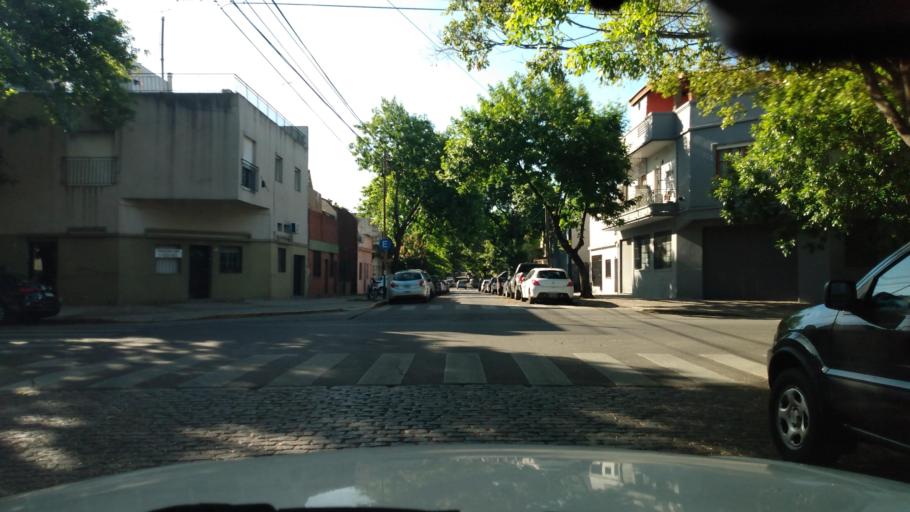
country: AR
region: Buenos Aires F.D.
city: Villa Santa Rita
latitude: -34.5850
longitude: -58.4832
